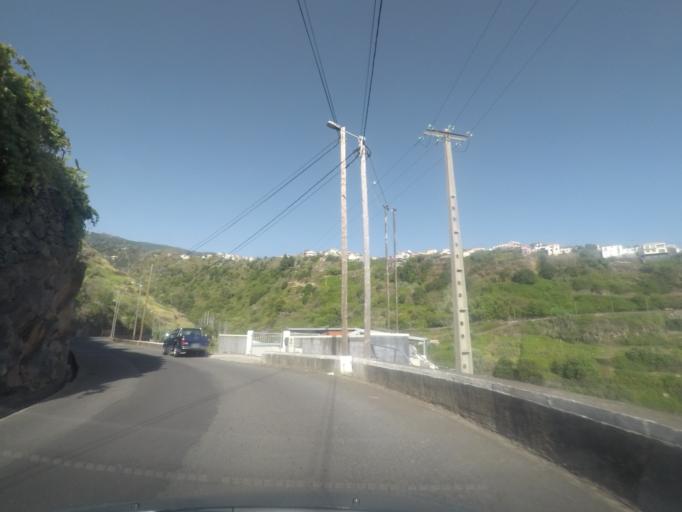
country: PT
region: Madeira
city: Calheta
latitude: 32.7294
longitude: -17.1677
